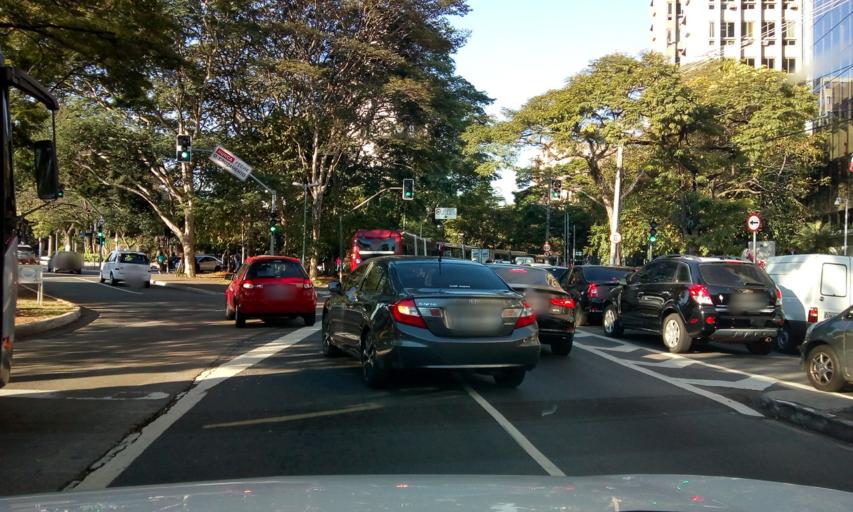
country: BR
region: Sao Paulo
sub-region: Sao Paulo
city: Sao Paulo
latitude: -23.5773
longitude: -46.6734
